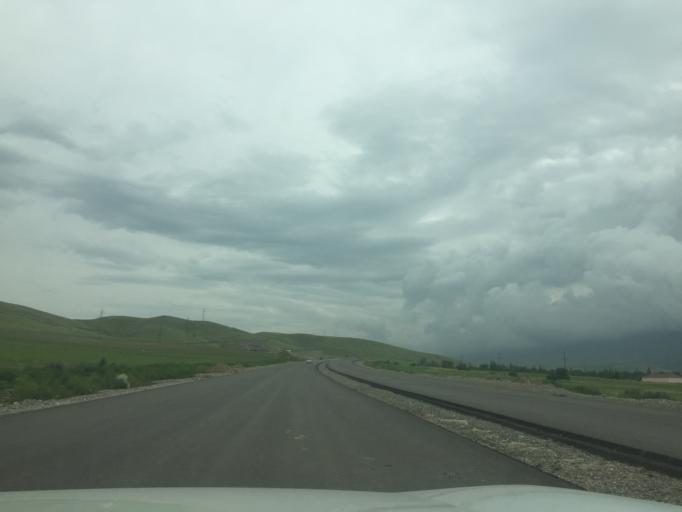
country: KZ
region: Ongtustik Qazaqstan
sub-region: Tulkibas Audany
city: Zhabagly
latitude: 42.5176
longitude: 70.5508
